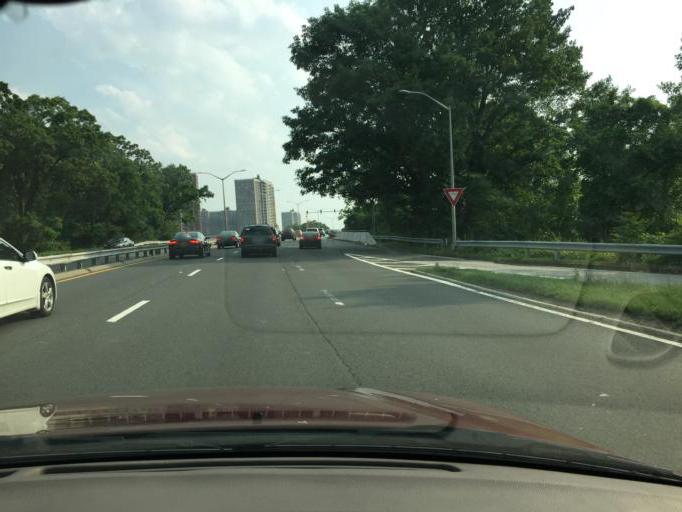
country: US
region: New York
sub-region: Bronx
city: Eastchester
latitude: 40.8707
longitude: -73.8195
